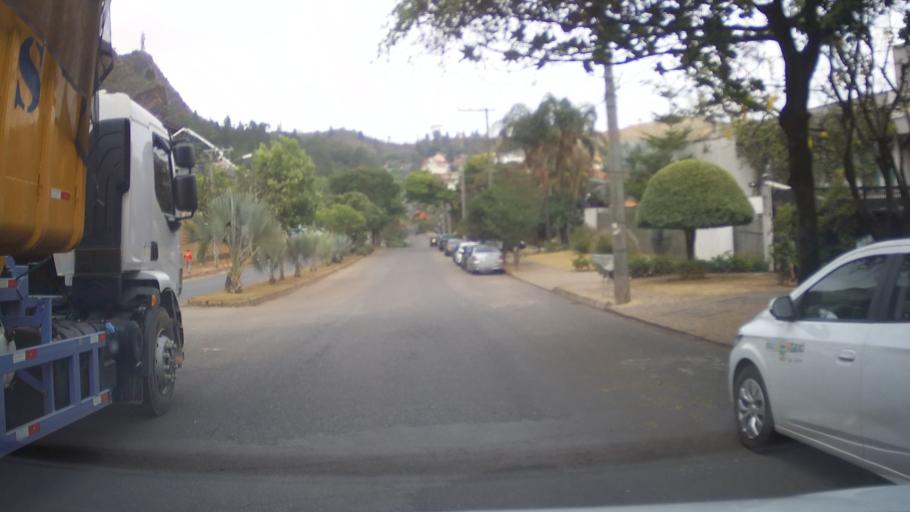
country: BR
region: Minas Gerais
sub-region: Belo Horizonte
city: Belo Horizonte
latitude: -19.9579
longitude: -43.9122
